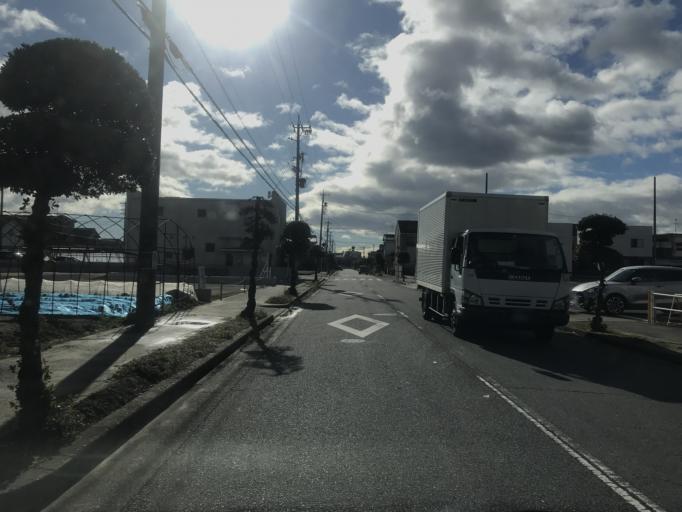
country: JP
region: Aichi
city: Nagoya-shi
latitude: 35.2043
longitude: 136.8441
